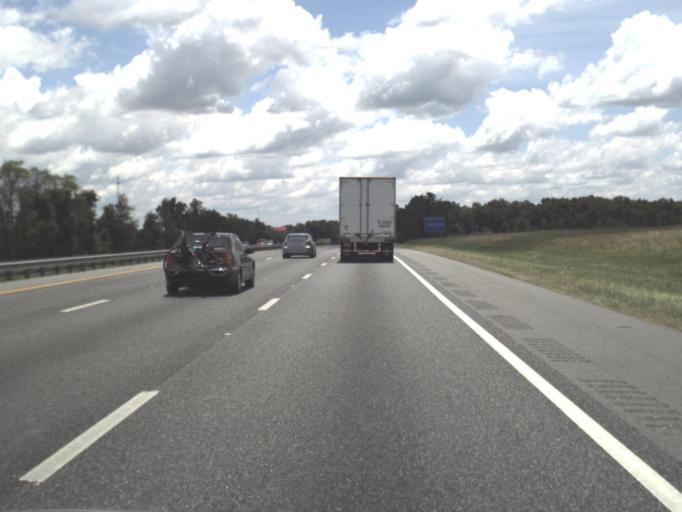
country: US
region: Florida
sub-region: Alachua County
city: High Springs
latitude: 30.0092
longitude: -82.6054
